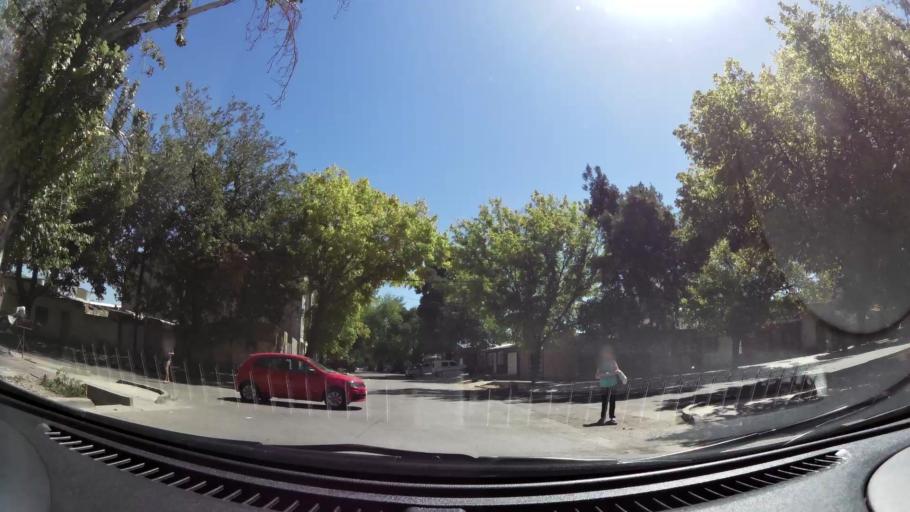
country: AR
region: Mendoza
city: Mendoza
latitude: -32.8758
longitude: -68.8205
